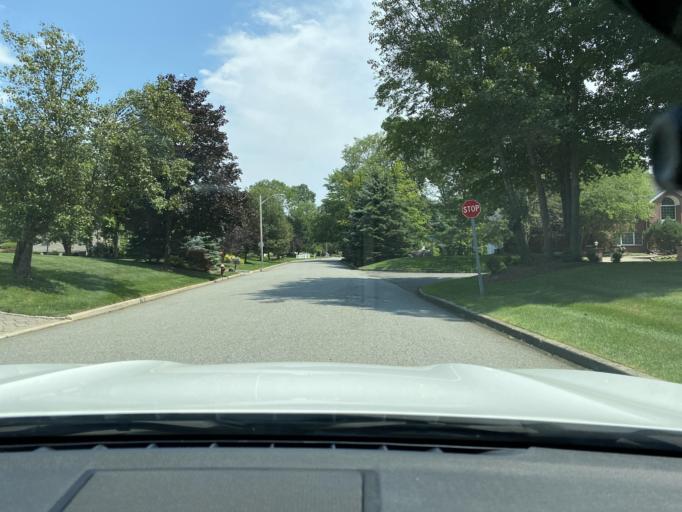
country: US
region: New York
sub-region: Rockland County
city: Airmont
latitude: 41.0887
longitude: -74.1209
